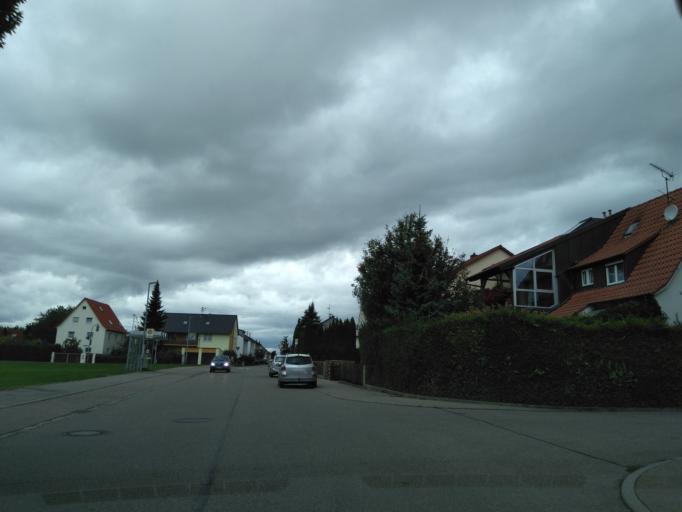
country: DE
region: Baden-Wuerttemberg
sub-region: Regierungsbezirk Stuttgart
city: Markgroningen
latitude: 48.9077
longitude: 9.0790
